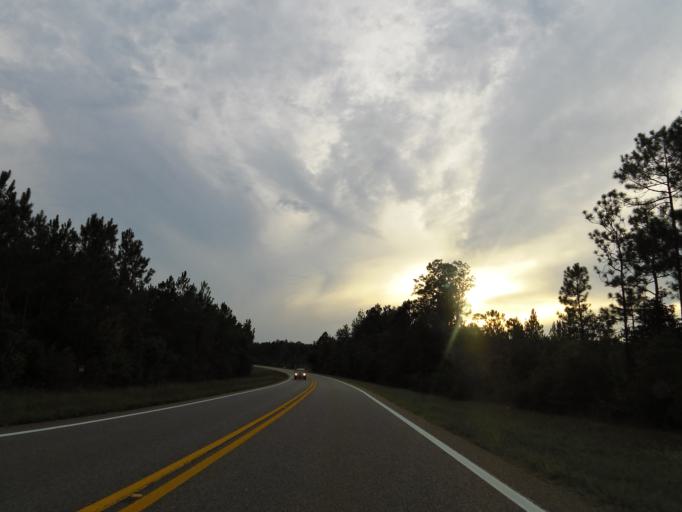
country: US
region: Alabama
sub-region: Baldwin County
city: Bay Minette
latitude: 30.9511
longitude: -87.6653
